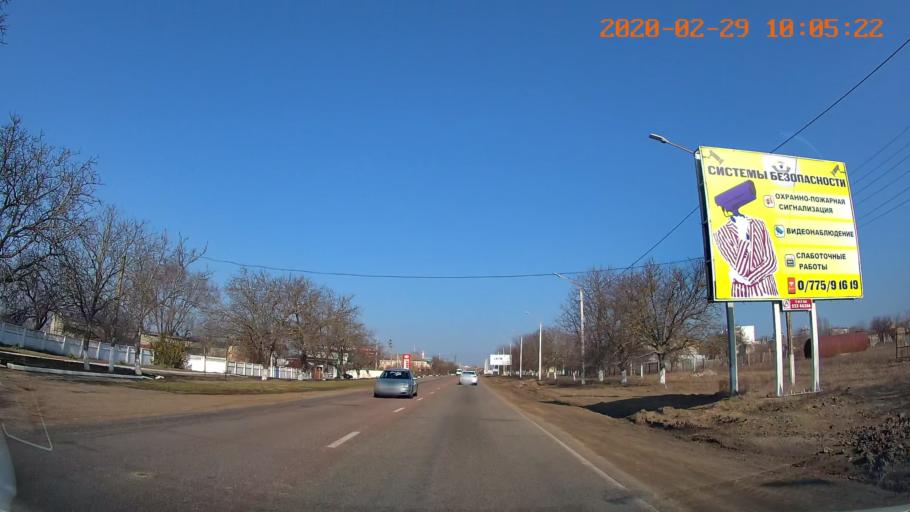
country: MD
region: Telenesti
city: Tiraspolul Nou
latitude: 46.8066
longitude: 29.6718
